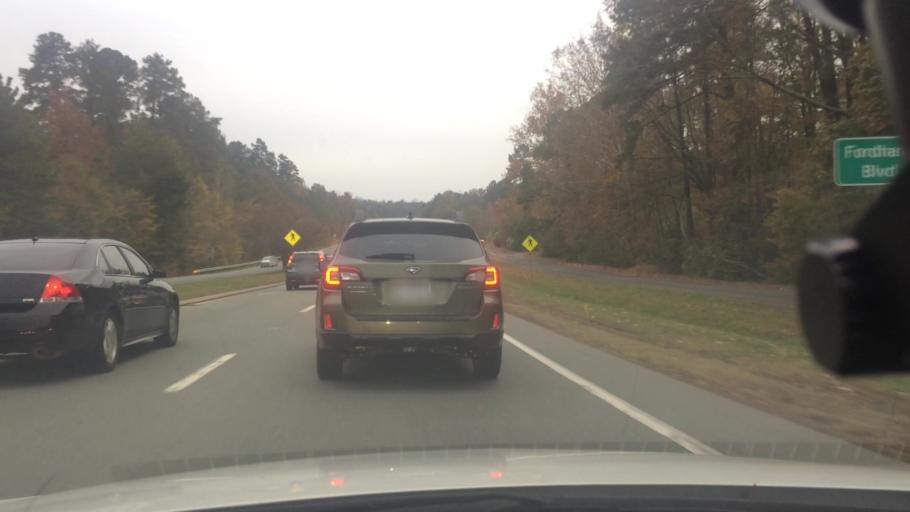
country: US
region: North Carolina
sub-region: Orange County
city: Chapel Hill
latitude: 35.9066
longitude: -79.0286
